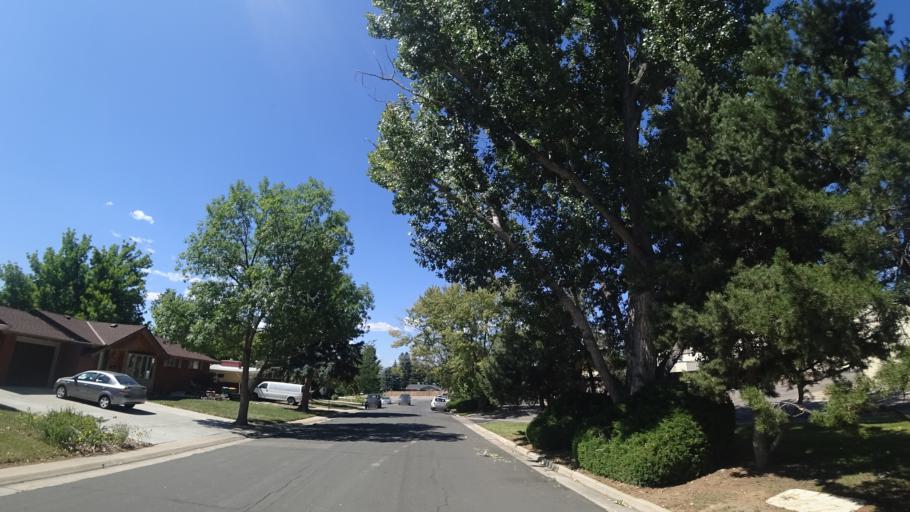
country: US
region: Colorado
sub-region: Arapahoe County
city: Greenwood Village
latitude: 39.6074
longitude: -104.9586
